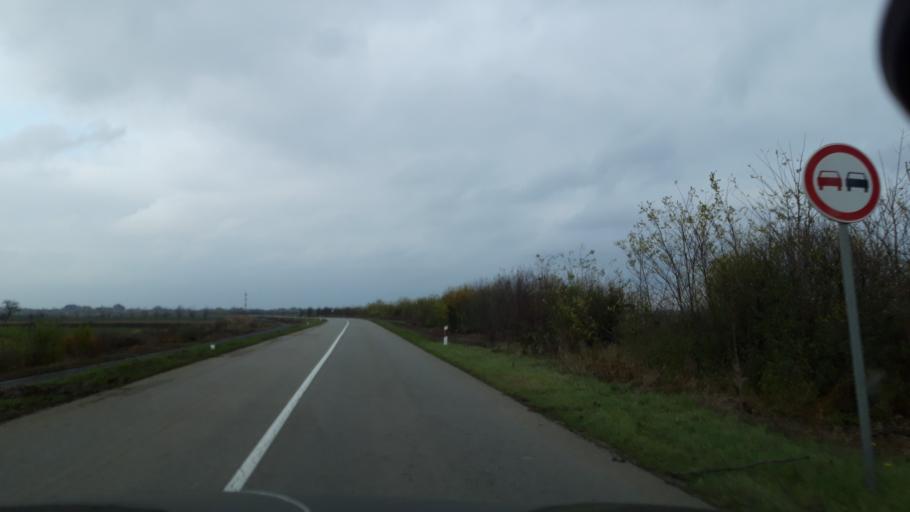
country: RS
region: Autonomna Pokrajina Vojvodina
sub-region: Severnobanatski Okrug
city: Novi Knezevac
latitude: 46.1113
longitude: 20.1027
